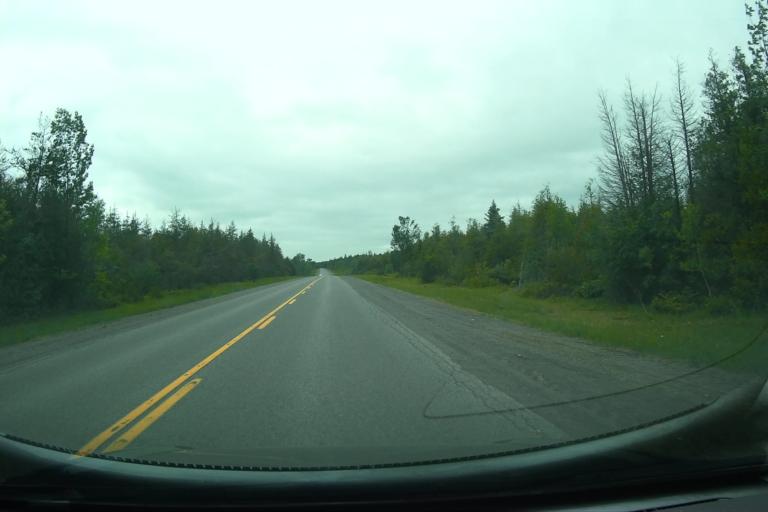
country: CA
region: Ontario
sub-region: Lanark County
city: Smiths Falls
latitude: 45.0102
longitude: -75.8333
